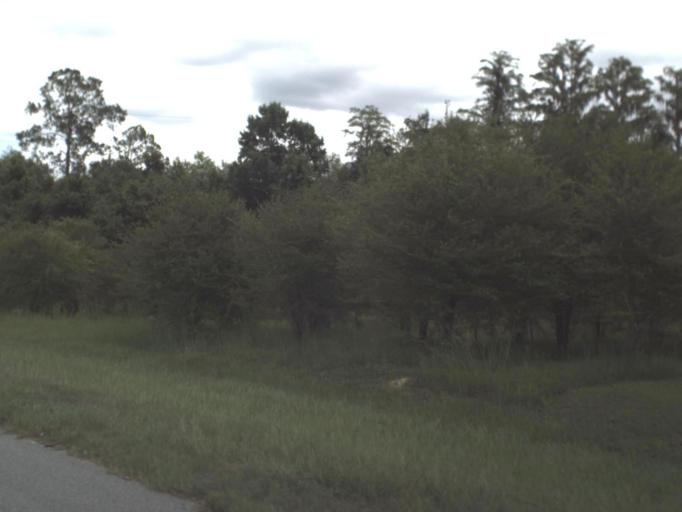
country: US
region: Florida
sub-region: Madison County
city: Madison
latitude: 30.6135
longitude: -83.3348
